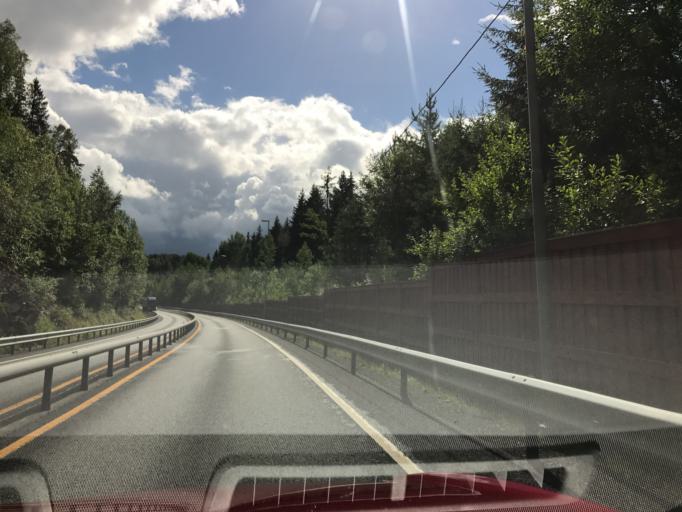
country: NO
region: Aust-Agder
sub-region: Gjerstad
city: Gjerstad
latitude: 58.8384
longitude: 9.0951
